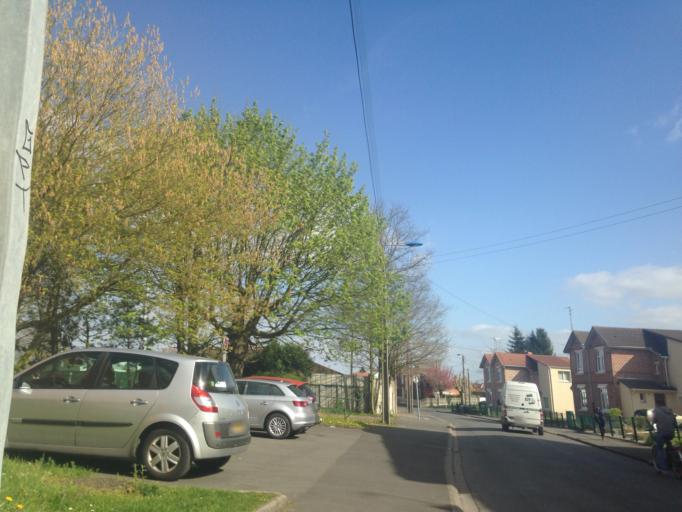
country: FR
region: Nord-Pas-de-Calais
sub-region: Departement du Pas-de-Calais
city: Avion
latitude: 50.4071
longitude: 2.8393
